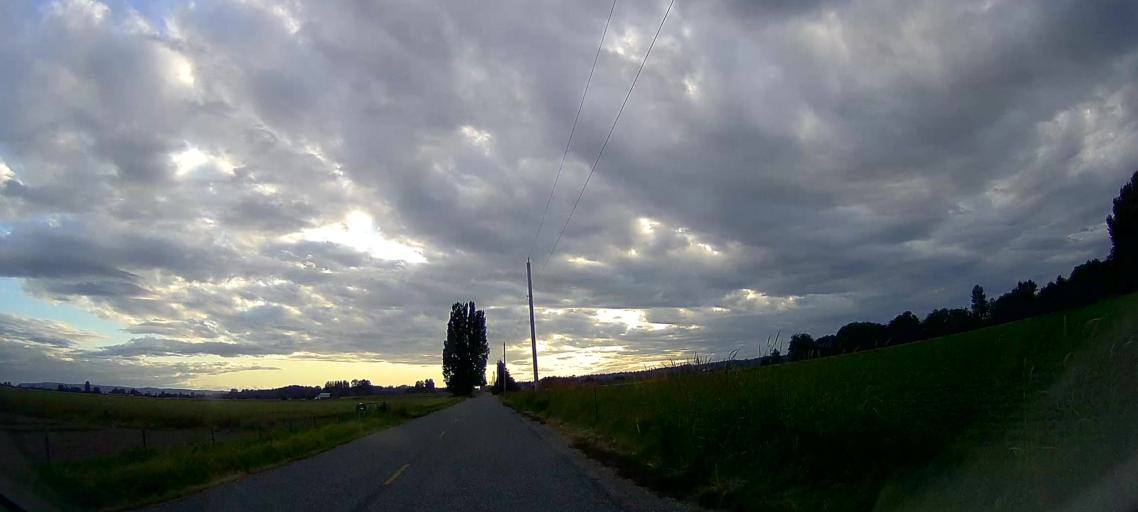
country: US
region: Washington
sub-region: Skagit County
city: Mount Vernon
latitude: 48.3702
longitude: -122.3839
